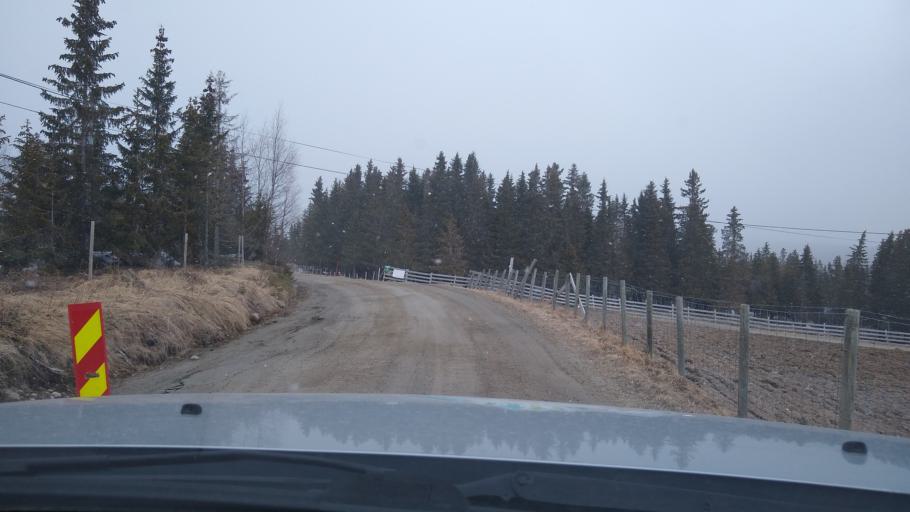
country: NO
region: Oppland
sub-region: Oyer
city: Tretten
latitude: 61.4610
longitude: 10.3399
